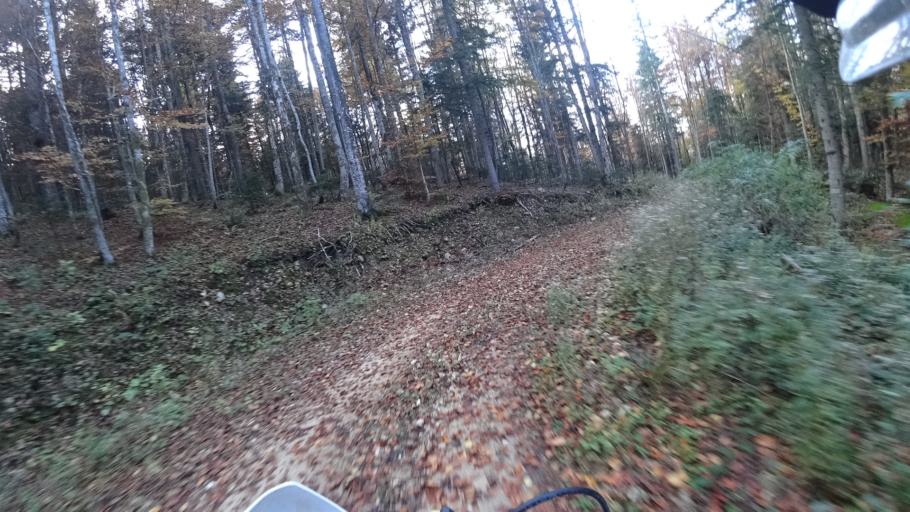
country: HR
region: Karlovacka
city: Plaski
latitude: 44.9642
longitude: 15.3952
